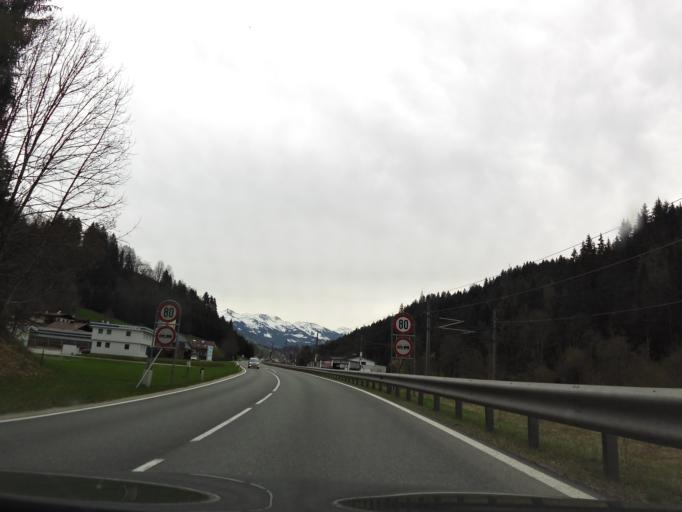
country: AT
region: Tyrol
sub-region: Politischer Bezirk Kitzbuhel
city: Itter
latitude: 47.4638
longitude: 12.1396
